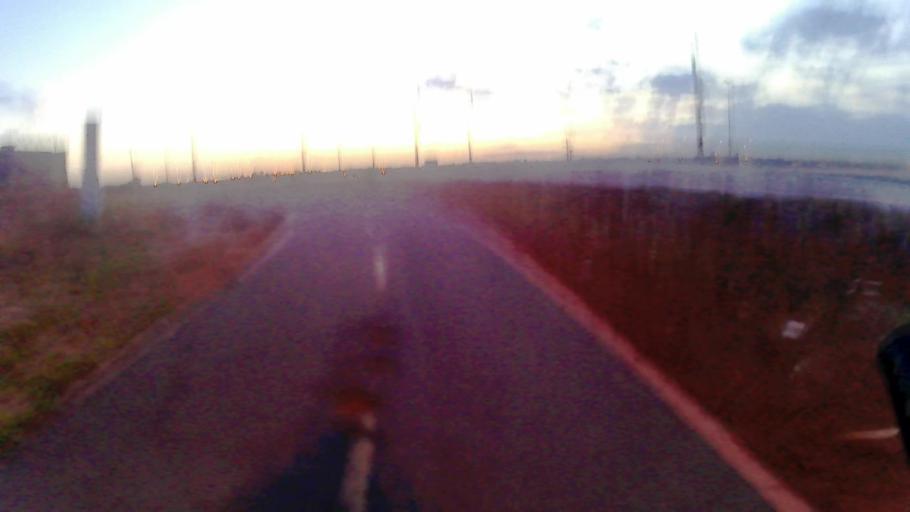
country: BR
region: Federal District
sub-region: Brasilia
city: Brasilia
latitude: -15.8682
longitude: -47.9904
